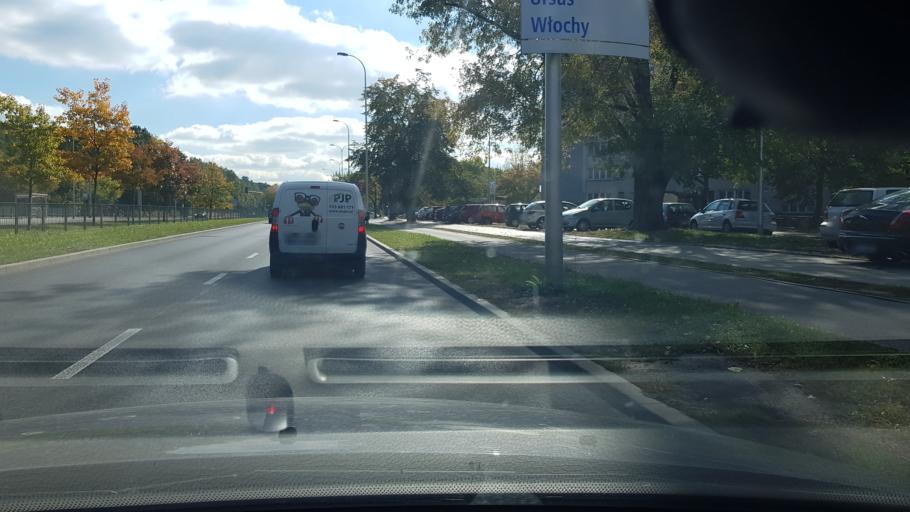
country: PL
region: Masovian Voivodeship
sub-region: Warszawa
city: Bielany
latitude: 52.2963
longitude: 20.9439
